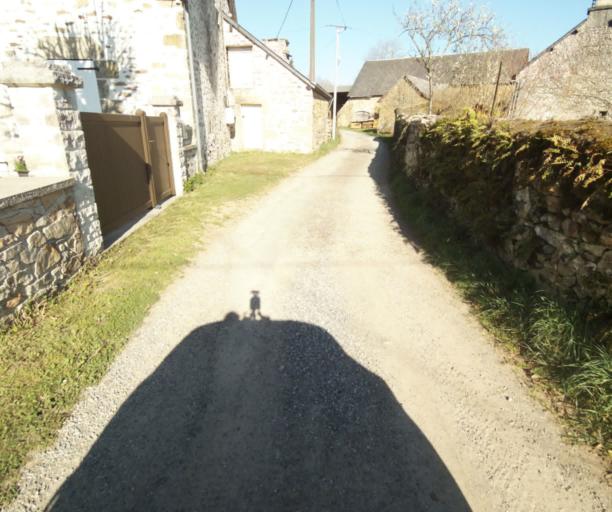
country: FR
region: Limousin
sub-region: Departement de la Correze
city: Chamboulive
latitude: 45.4833
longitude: 1.6998
